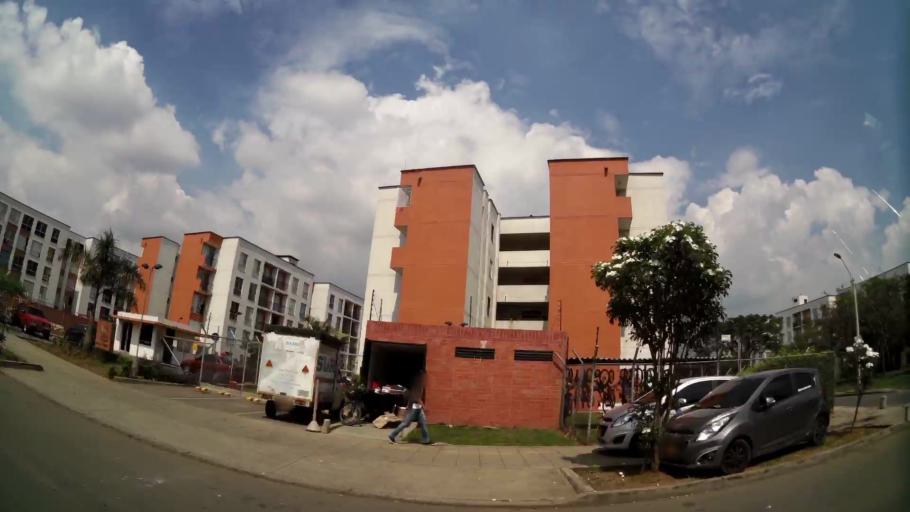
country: CO
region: Valle del Cauca
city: Cali
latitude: 3.4966
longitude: -76.4986
